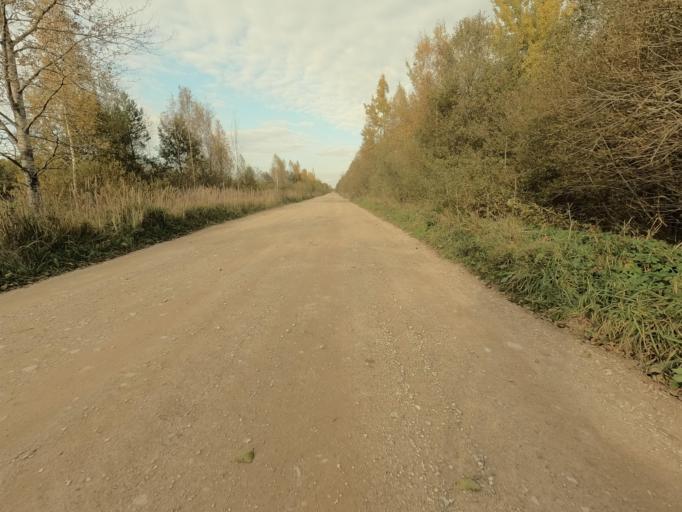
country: RU
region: Novgorod
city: Volkhovskiy
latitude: 58.9073
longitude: 31.0375
